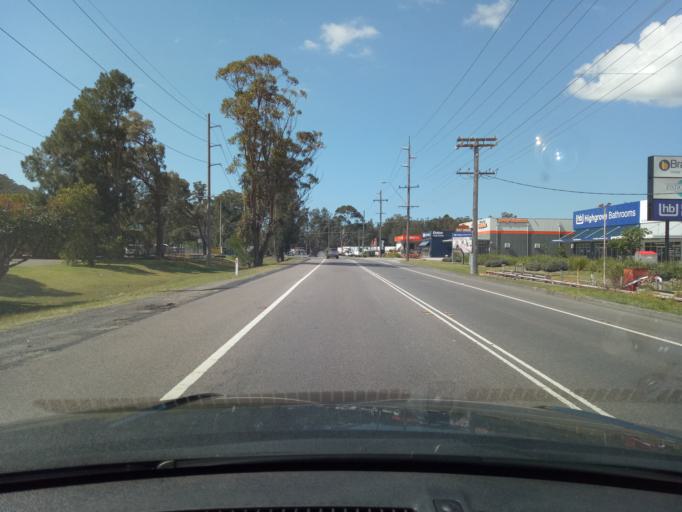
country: AU
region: New South Wales
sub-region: Gosford Shire
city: Gosford
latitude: -33.4157
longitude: 151.3303
